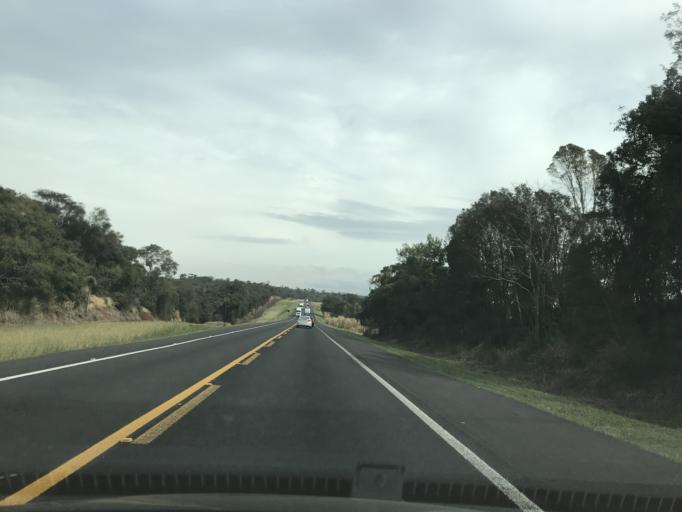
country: BR
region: Parana
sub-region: Matelandia
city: Matelandia
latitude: -25.1098
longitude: -53.7899
